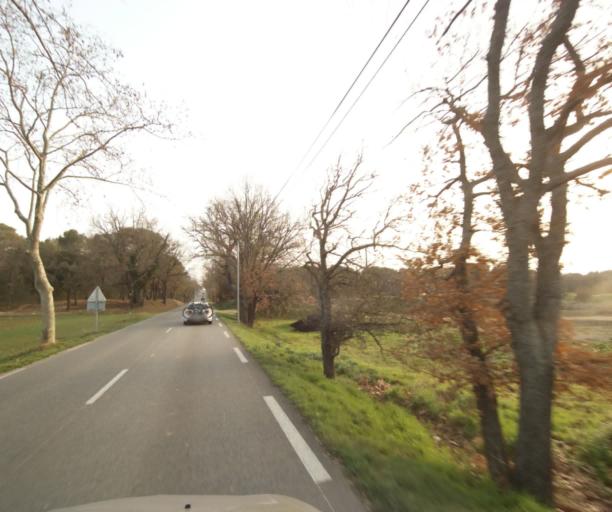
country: FR
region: Provence-Alpes-Cote d'Azur
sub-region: Departement des Bouches-du-Rhone
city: Eguilles
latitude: 43.6008
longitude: 5.3661
